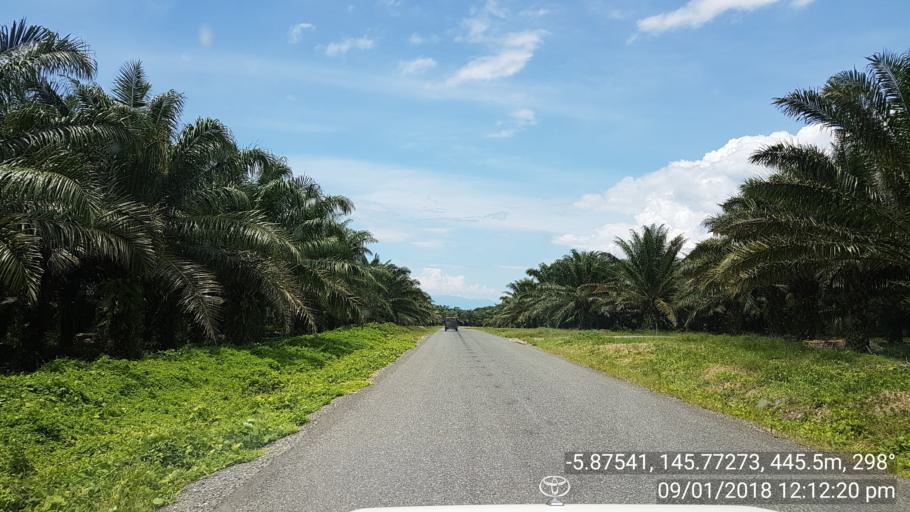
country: PG
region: Eastern Highlands
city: Kainantu
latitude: -5.8752
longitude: 145.7727
